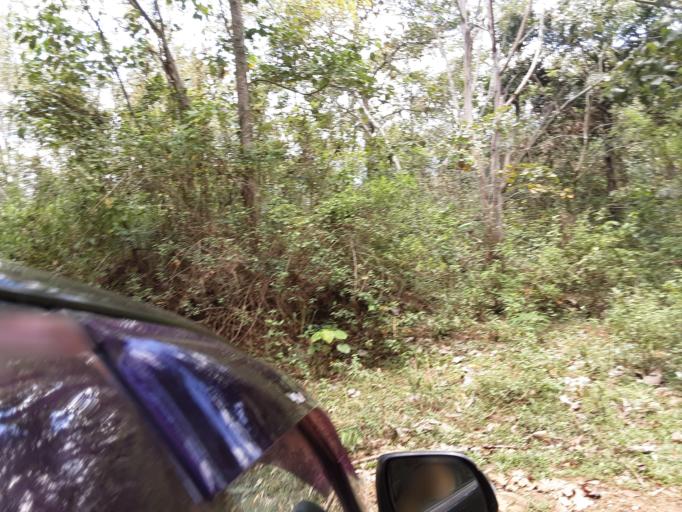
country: LK
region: Uva
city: Haputale
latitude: 6.8180
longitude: 81.1095
